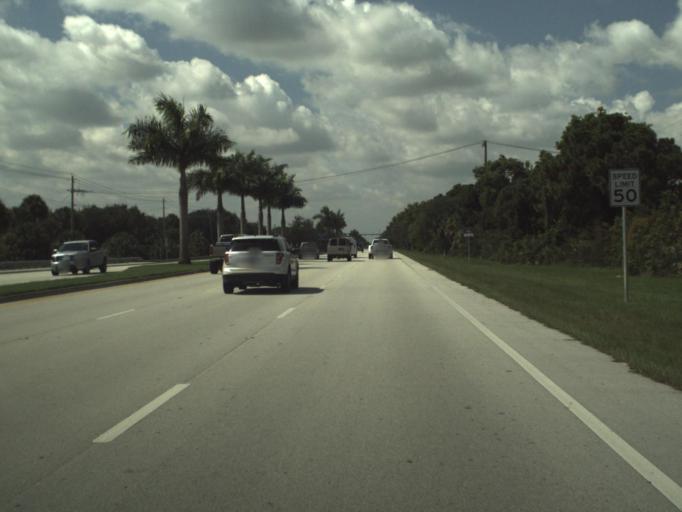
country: US
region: Florida
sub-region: Palm Beach County
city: Jupiter
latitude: 26.9254
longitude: -80.0939
